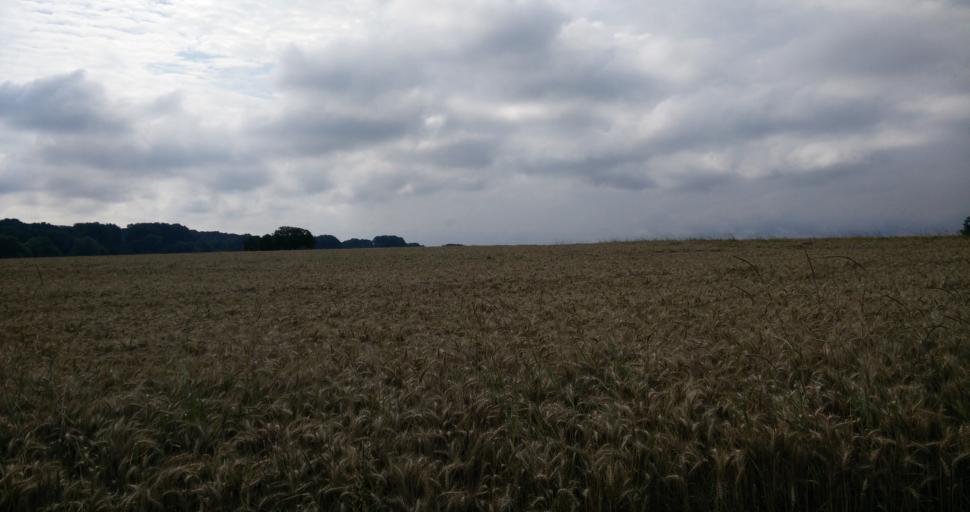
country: DE
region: Rheinland-Pfalz
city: Barbelroth
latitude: 49.1087
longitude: 8.0685
